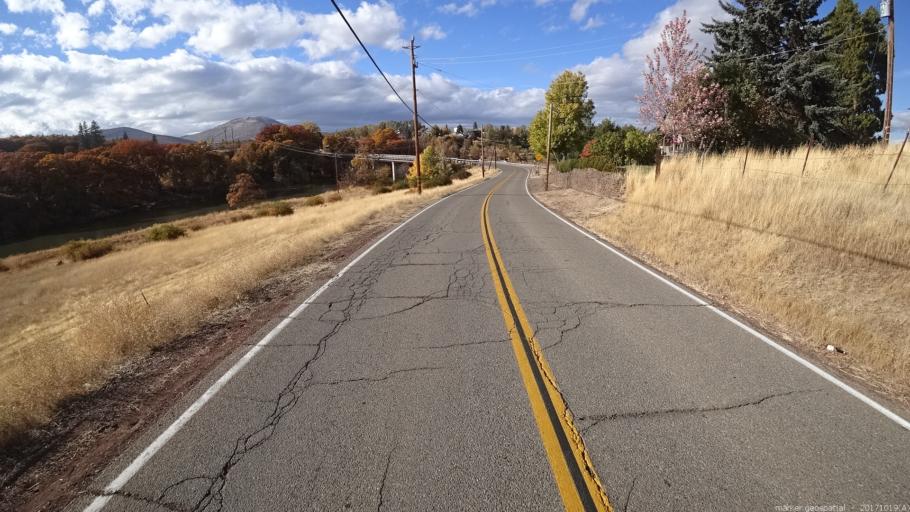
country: US
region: California
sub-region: Shasta County
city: Burney
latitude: 41.0000
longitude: -121.4347
